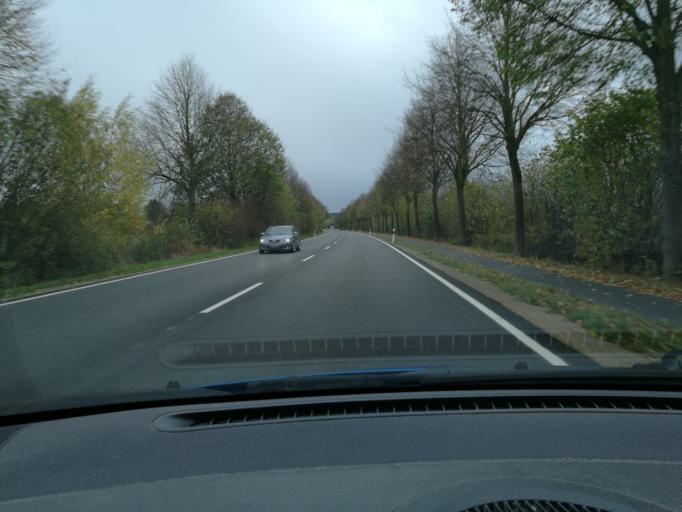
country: DE
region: Schleswig-Holstein
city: Fredeburg
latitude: 53.6833
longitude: 10.7289
